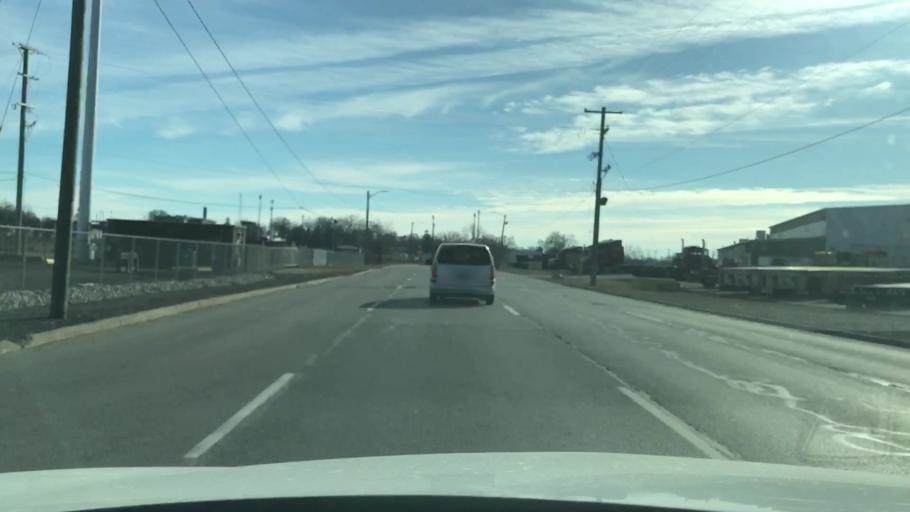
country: US
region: Michigan
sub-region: Oakland County
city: Pontiac
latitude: 42.6509
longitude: -83.3110
